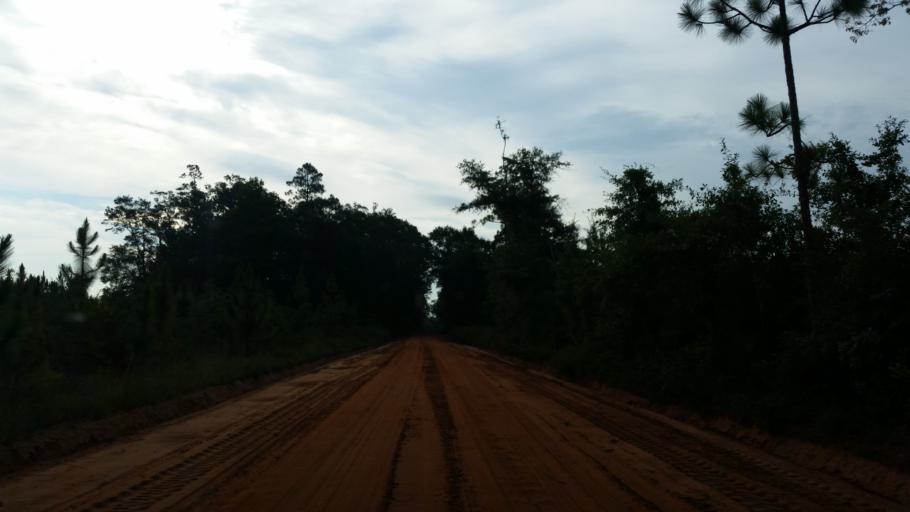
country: US
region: Alabama
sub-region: Escambia County
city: Atmore
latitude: 30.7934
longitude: -87.5432
